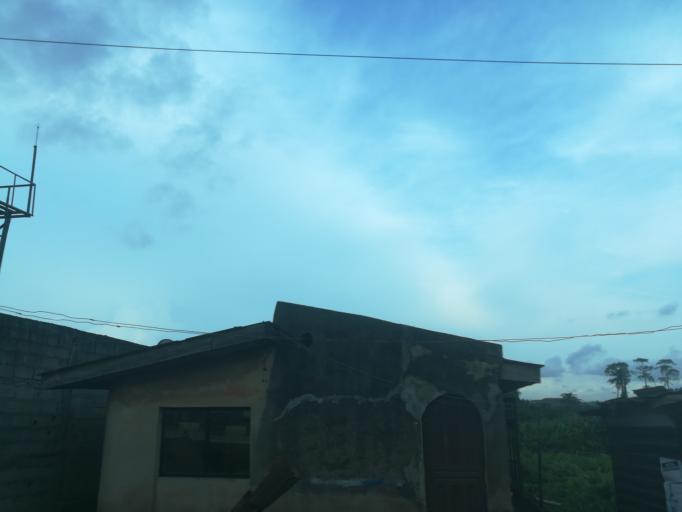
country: NG
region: Lagos
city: Ebute Ikorodu
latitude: 6.6167
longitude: 3.4754
